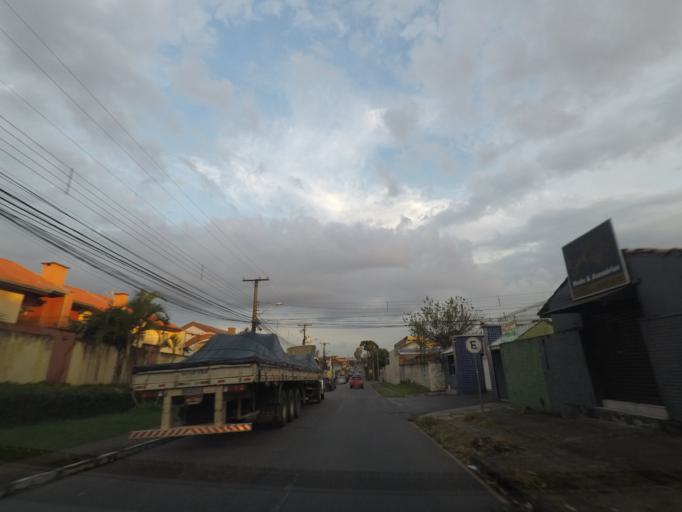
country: BR
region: Parana
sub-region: Sao Jose Dos Pinhais
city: Sao Jose dos Pinhais
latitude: -25.5037
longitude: -49.2514
